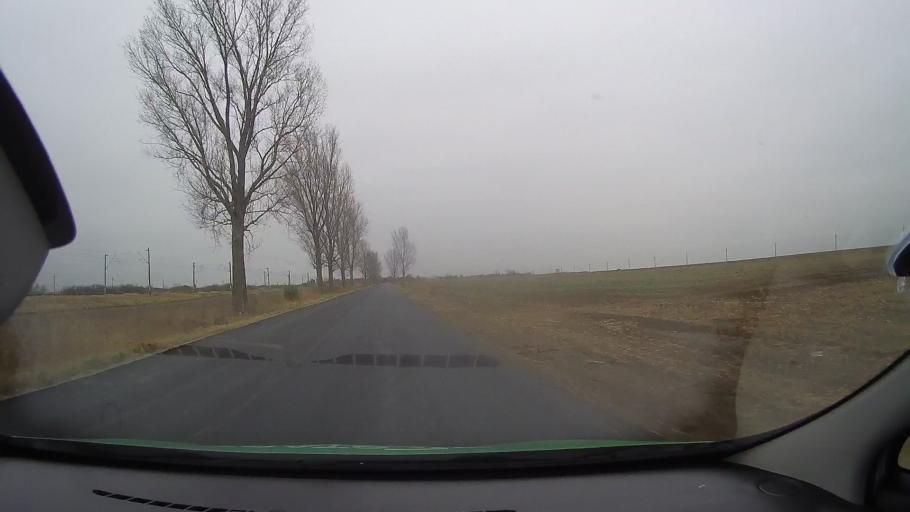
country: RO
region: Ialomita
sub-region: Comuna Valea Ciorii
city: Valea Ciorii
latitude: 44.7337
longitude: 27.5803
